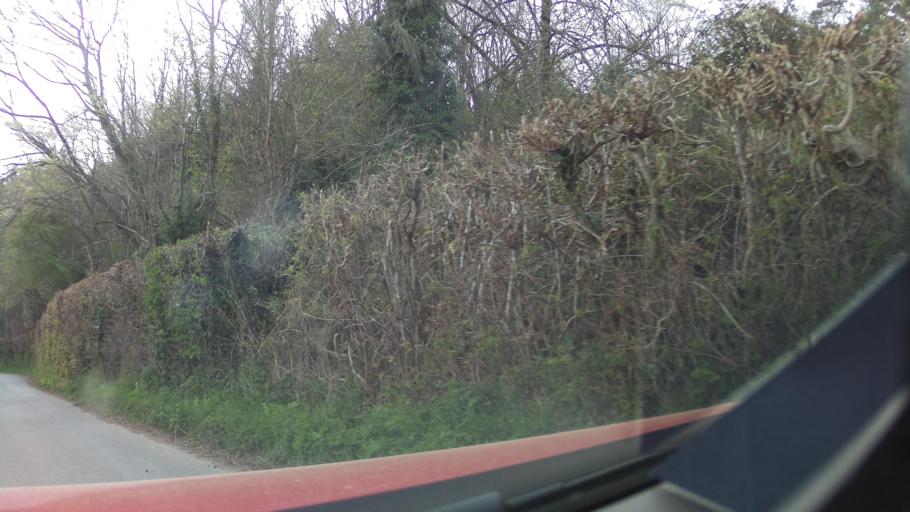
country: GB
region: England
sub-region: Somerset
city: Milborne Port
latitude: 50.9480
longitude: -2.4621
